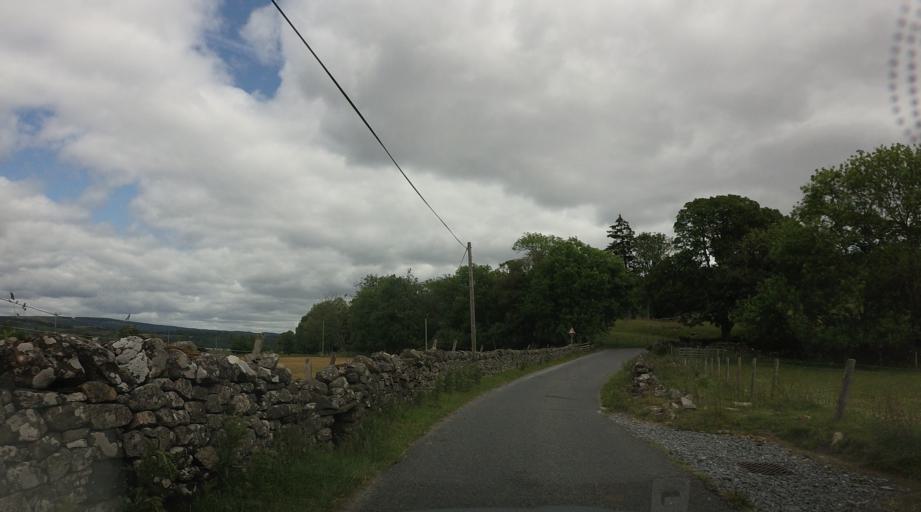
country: GB
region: Scotland
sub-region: Perth and Kinross
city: Aberfeldy
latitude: 56.6910
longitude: -4.1408
